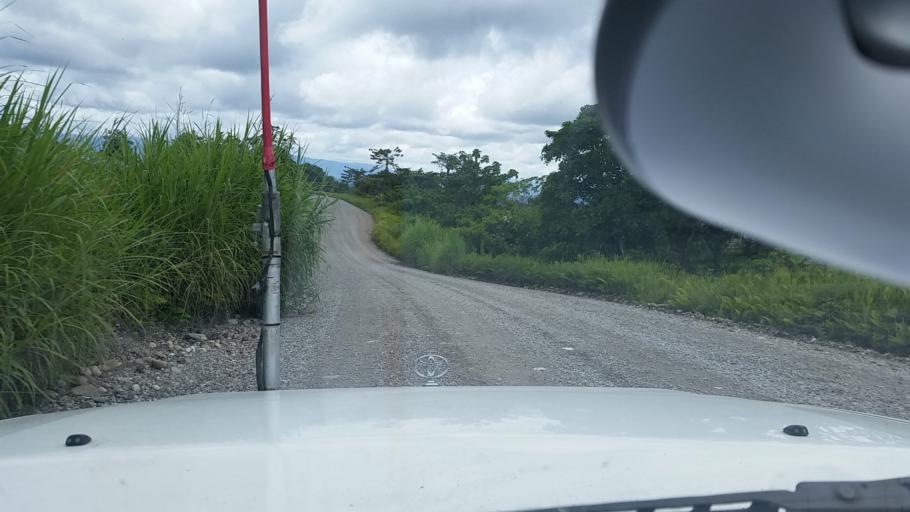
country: PG
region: Western Province
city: Kiunga
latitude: -5.5649
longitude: 141.2647
